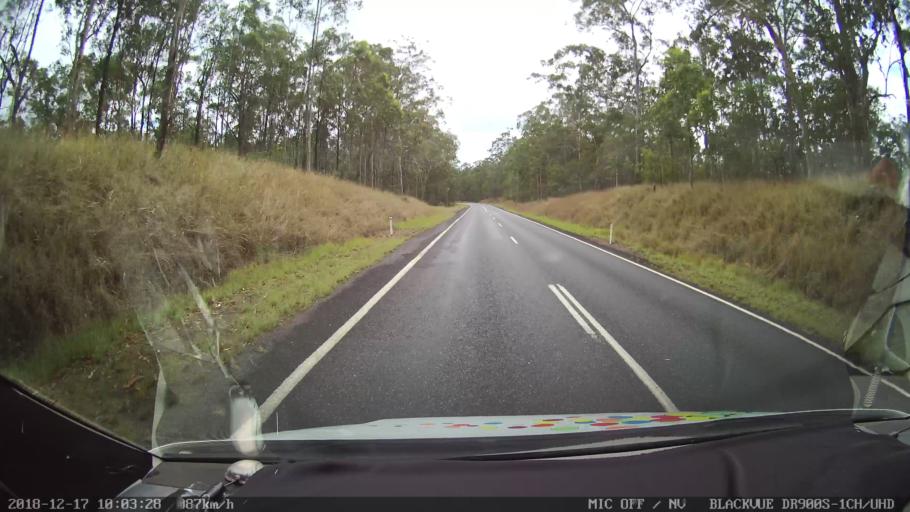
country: AU
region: New South Wales
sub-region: Tenterfield Municipality
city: Carrolls Creek
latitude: -28.8972
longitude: 152.4642
